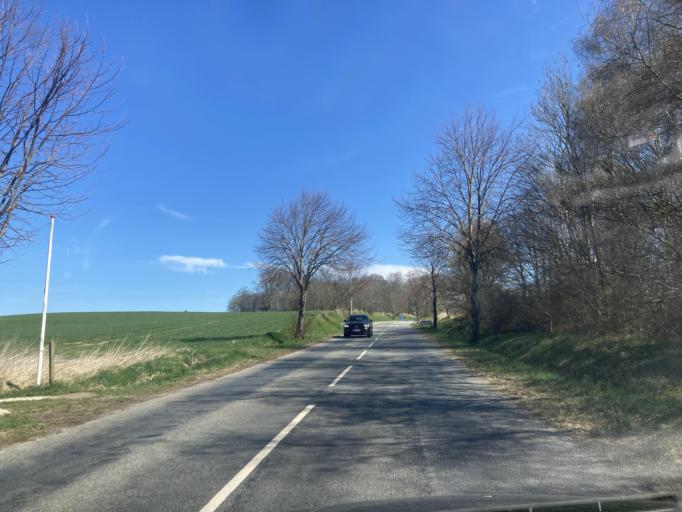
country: DK
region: Capital Region
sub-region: Gribskov Kommune
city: Helsinge
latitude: 56.0844
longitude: 12.1990
